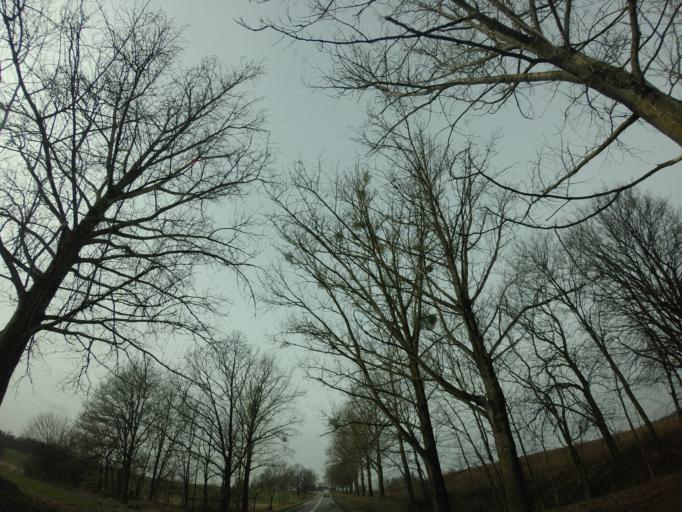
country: PL
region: West Pomeranian Voivodeship
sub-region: Powiat drawski
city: Drawsko Pomorskie
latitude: 53.5258
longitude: 15.8649
